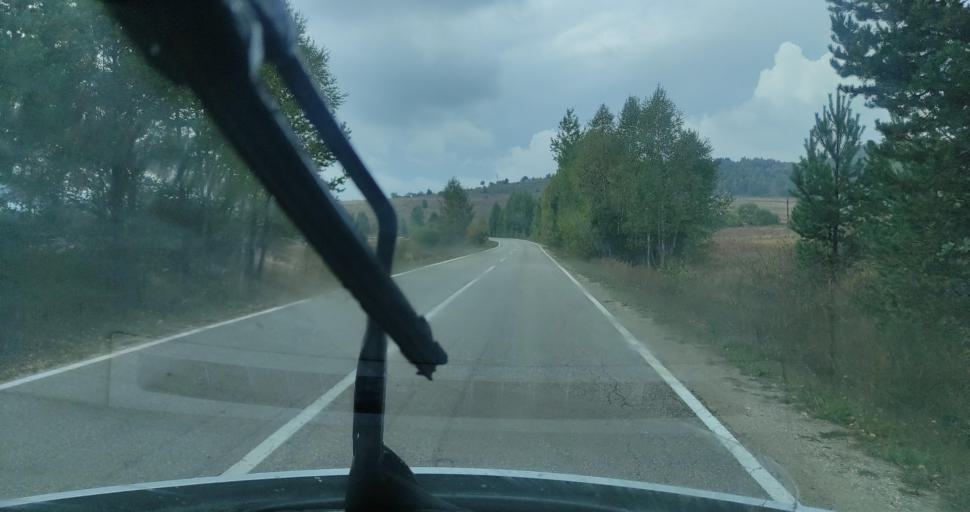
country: RS
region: Central Serbia
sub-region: Jablanicki Okrug
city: Crna Trava
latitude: 42.6955
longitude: 22.3251
